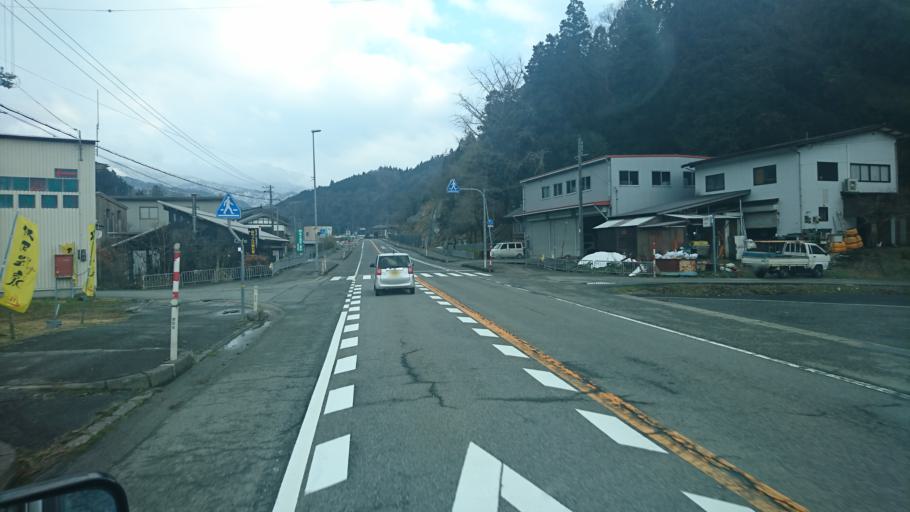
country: JP
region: Hyogo
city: Toyooka
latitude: 35.4761
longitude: 134.5866
